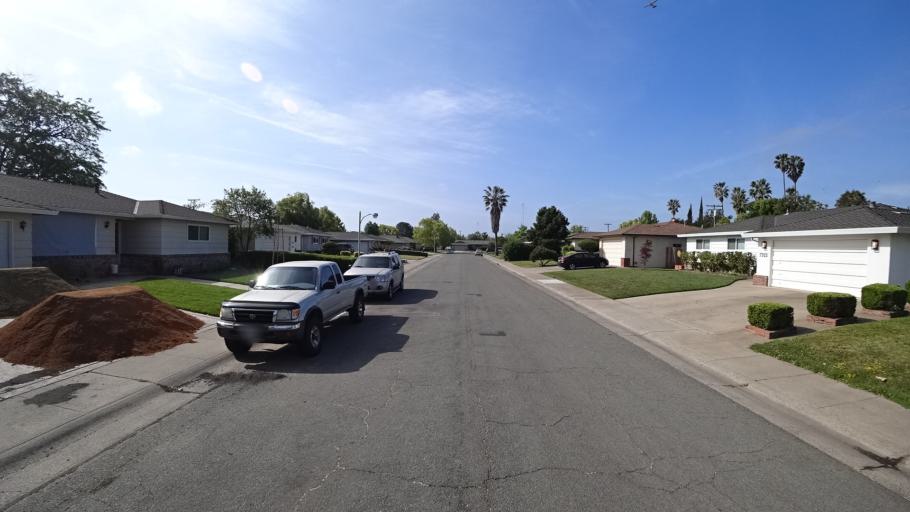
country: US
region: California
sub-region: Sacramento County
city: Parkway
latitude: 38.4914
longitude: -121.5103
